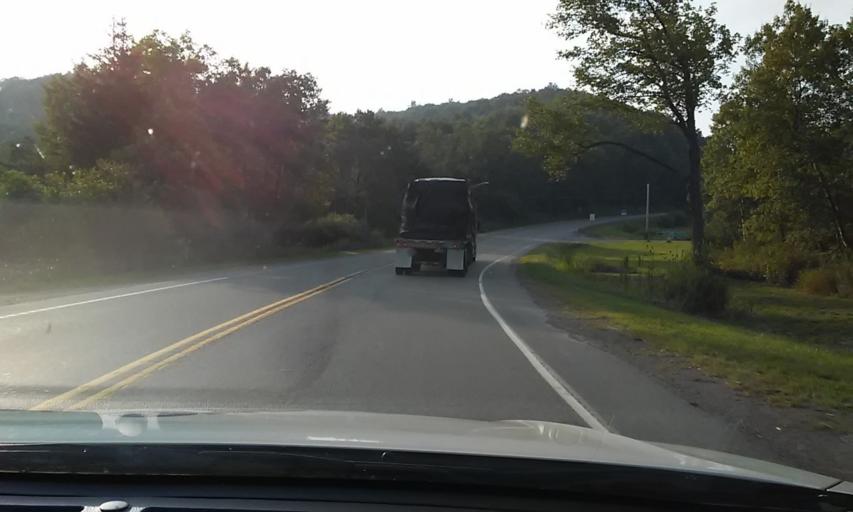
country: US
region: Pennsylvania
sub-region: McKean County
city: Smethport
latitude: 41.7055
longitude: -78.5925
